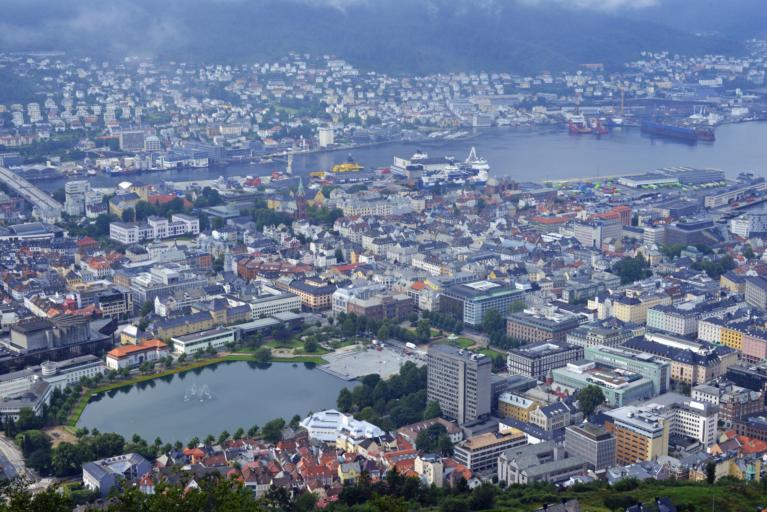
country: NO
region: Hordaland
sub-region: Bergen
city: Bergen
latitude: 60.3947
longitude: 5.3426
